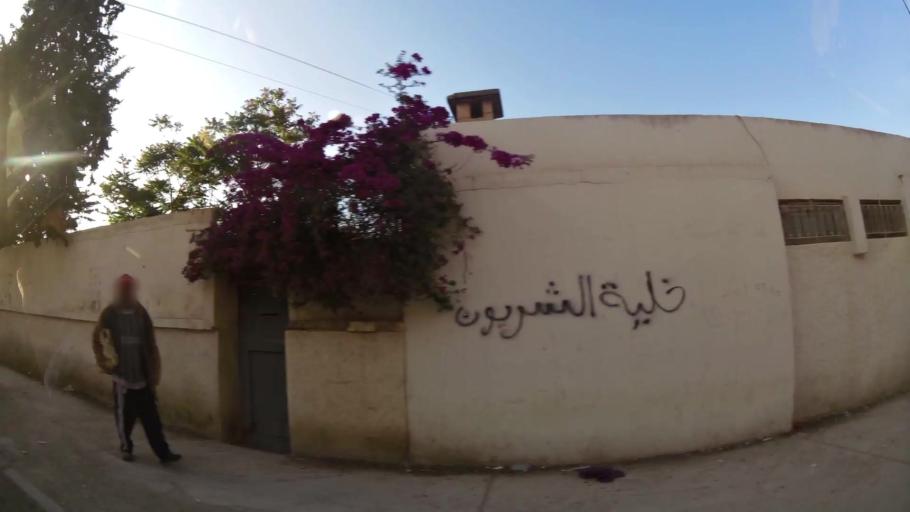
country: MA
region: Oriental
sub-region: Oujda-Angad
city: Oujda
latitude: 34.7043
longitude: -1.9058
